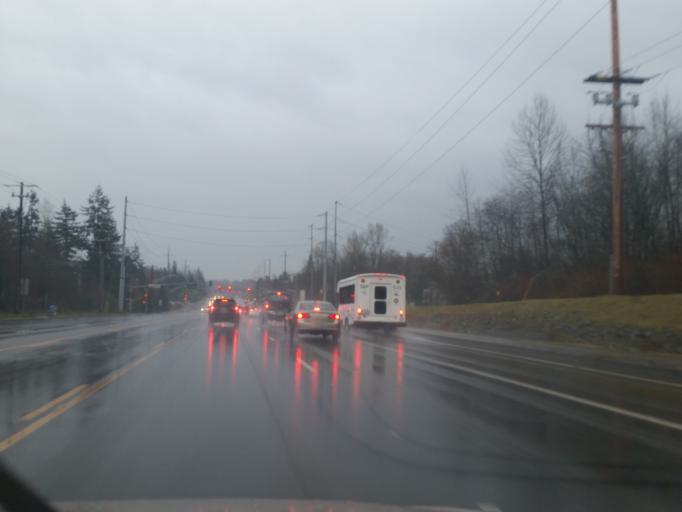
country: US
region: Washington
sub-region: Snohomish County
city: Martha Lake
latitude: 47.8998
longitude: -122.2660
